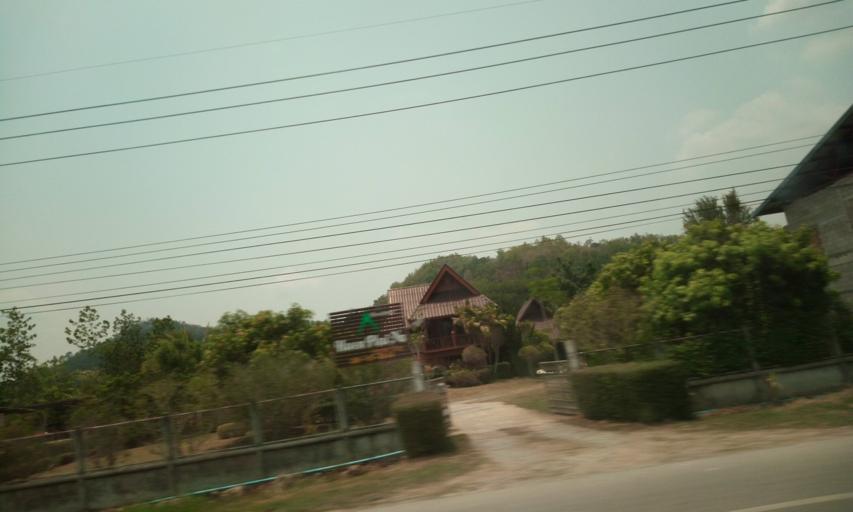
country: TH
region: Chiang Rai
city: Thoeng
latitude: 19.6895
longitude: 100.1440
